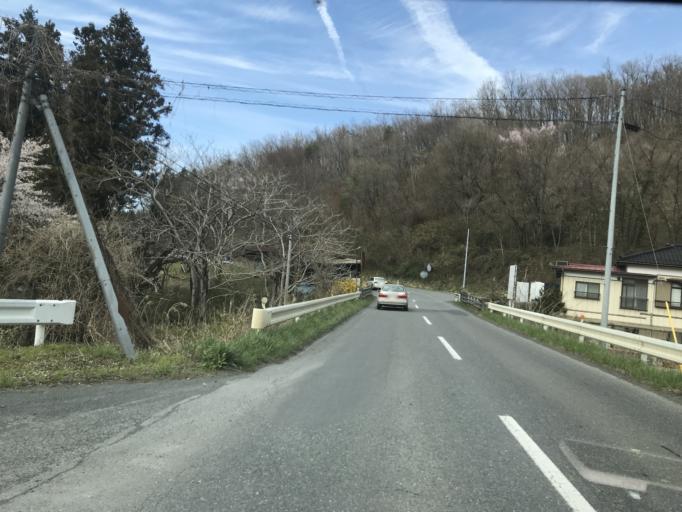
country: JP
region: Iwate
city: Ichinoseki
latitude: 38.8428
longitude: 141.3420
